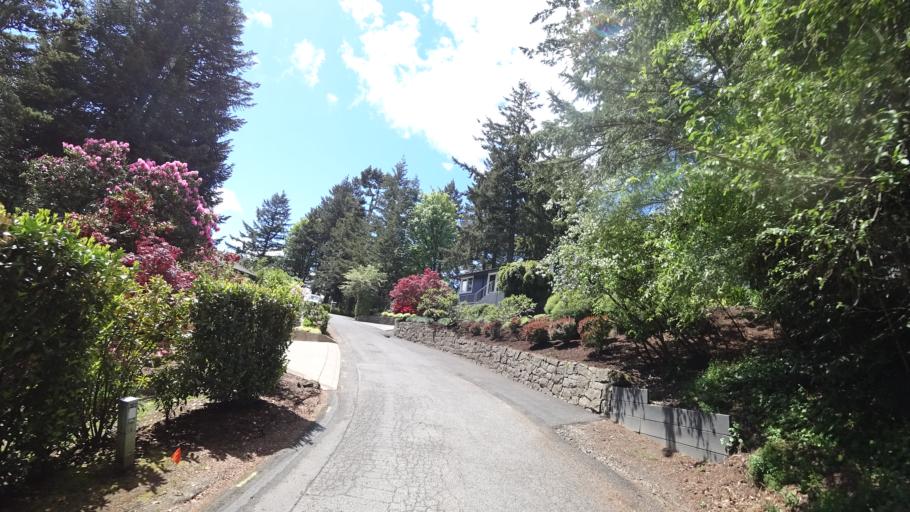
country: US
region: Oregon
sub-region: Washington County
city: West Slope
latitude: 45.5130
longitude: -122.7301
